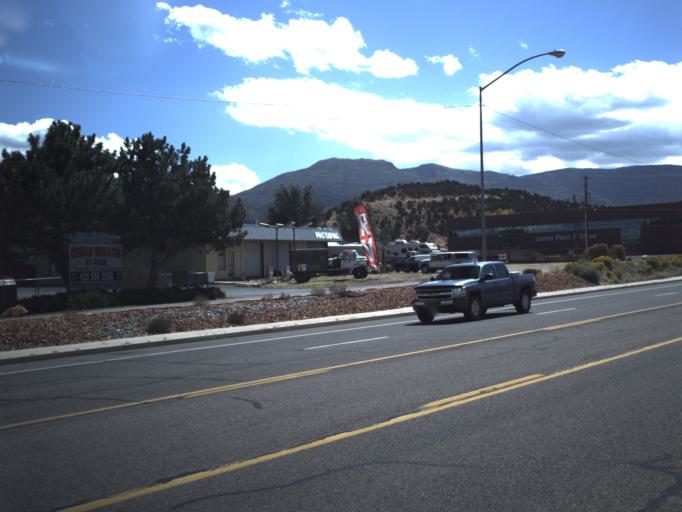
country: US
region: Utah
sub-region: Iron County
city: Cedar City
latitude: 37.7075
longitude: -113.0625
